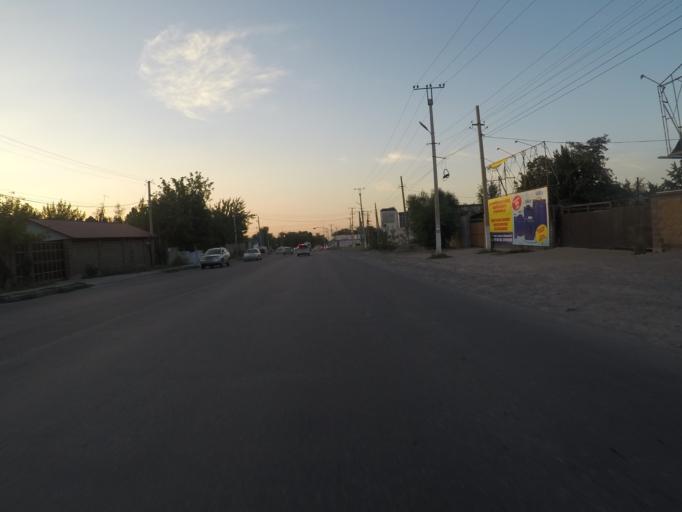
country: KG
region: Chuy
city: Lebedinovka
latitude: 42.8113
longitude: 74.6459
